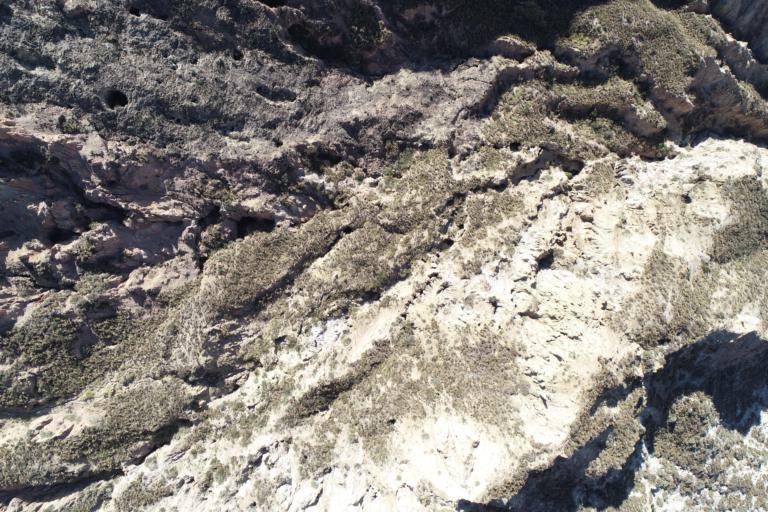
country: BO
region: La Paz
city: La Paz
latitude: -16.5509
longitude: -68.1068
